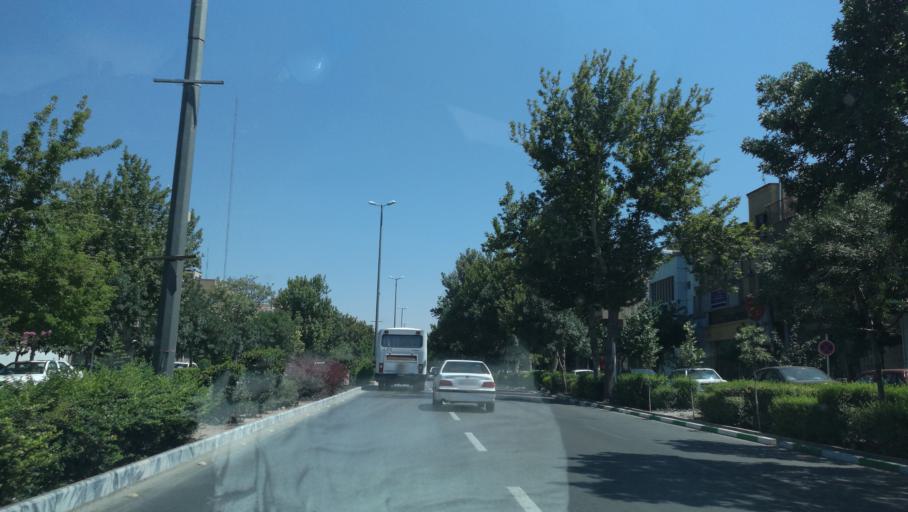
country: IR
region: Razavi Khorasan
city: Mashhad
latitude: 36.2728
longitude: 59.5939
